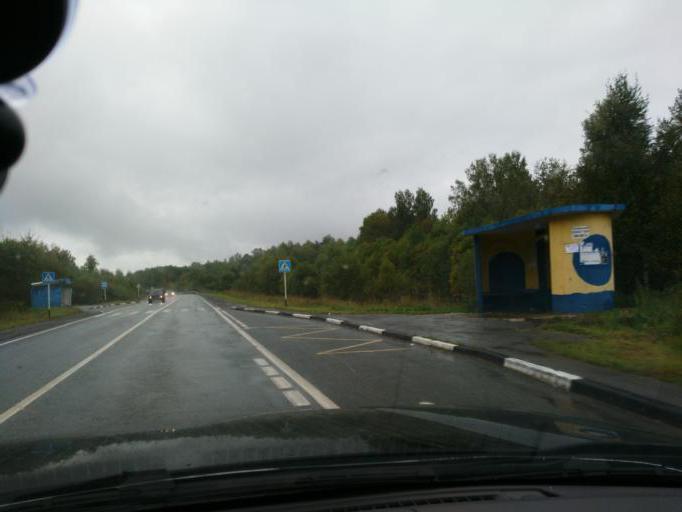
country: RU
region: Perm
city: Yugo-Kamskiy
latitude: 57.7309
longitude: 55.7014
